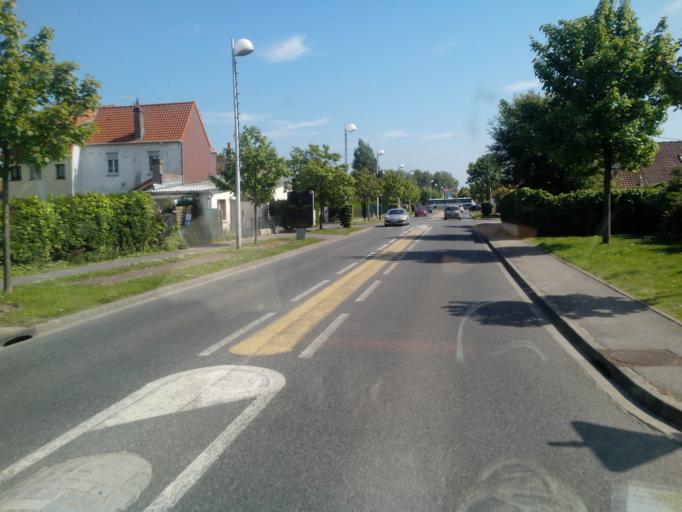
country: FR
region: Nord-Pas-de-Calais
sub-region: Departement du Pas-de-Calais
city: Berck
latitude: 50.4101
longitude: 1.5941
